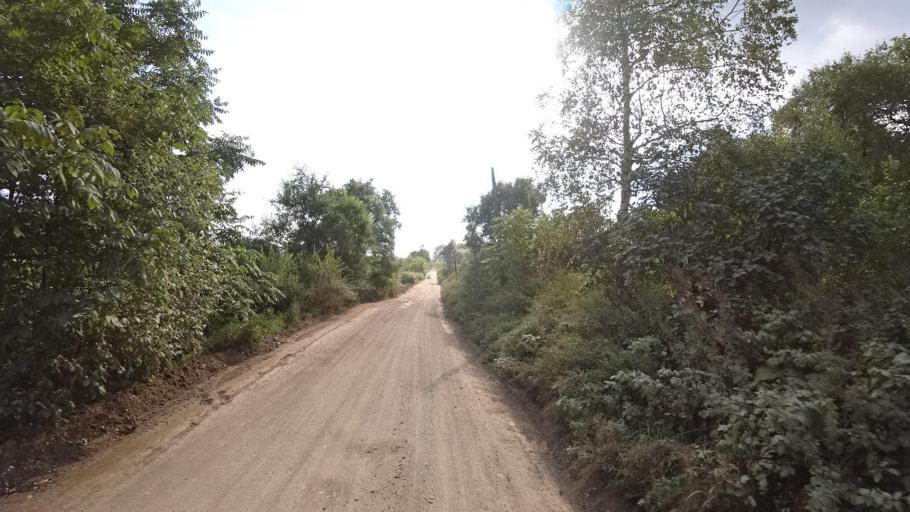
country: RU
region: Jewish Autonomous Oblast
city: Birakan
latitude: 49.0005
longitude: 131.7295
